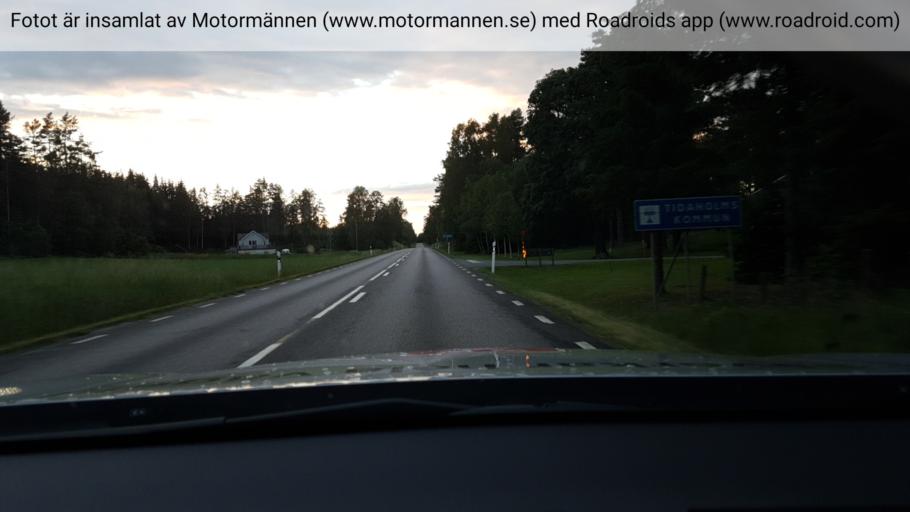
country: SE
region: Joenkoeping
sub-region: Mullsjo Kommun
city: Mullsjoe
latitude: 58.0553
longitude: 13.8048
